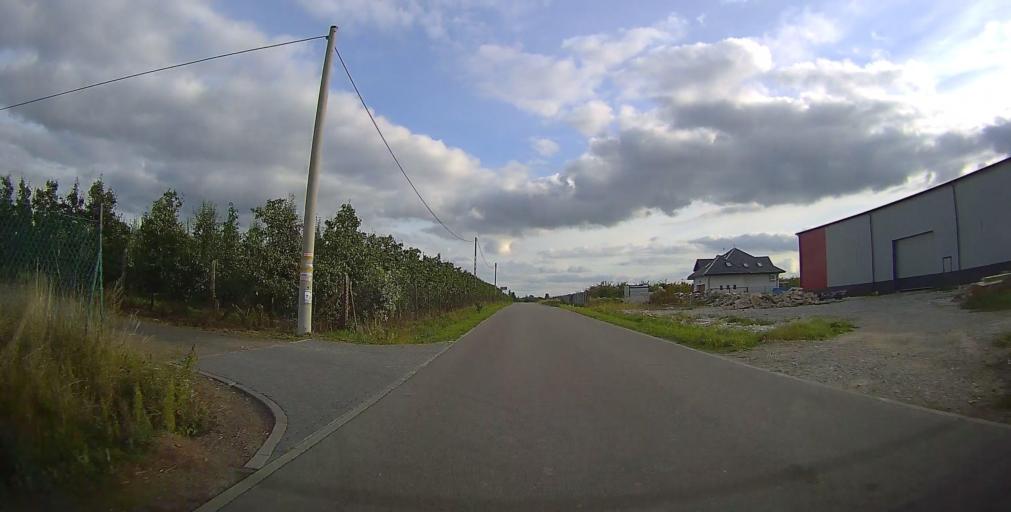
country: PL
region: Masovian Voivodeship
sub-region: Powiat grojecki
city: Jasieniec
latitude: 51.7530
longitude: 20.9622
